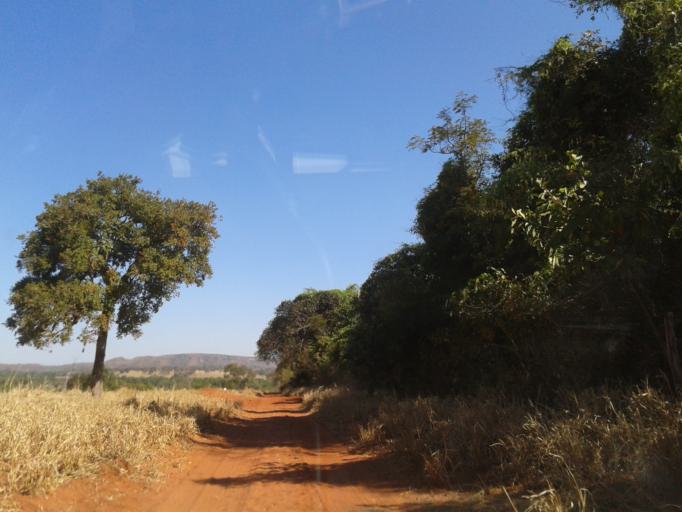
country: BR
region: Minas Gerais
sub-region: Santa Vitoria
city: Santa Vitoria
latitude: -19.1391
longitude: -50.0394
